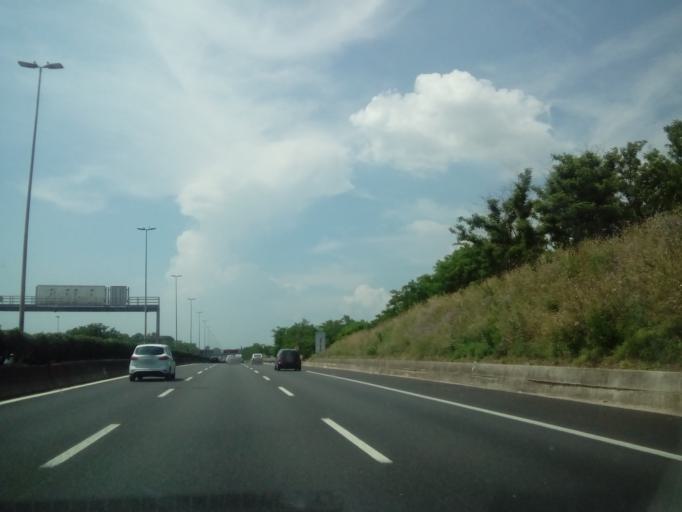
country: IT
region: Latium
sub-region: Citta metropolitana di Roma Capitale
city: Colle Verde
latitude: 41.9630
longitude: 12.5710
